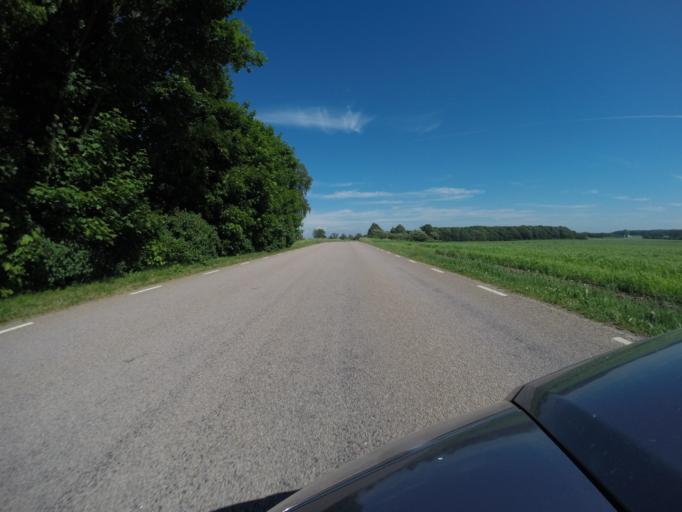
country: SE
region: Skane
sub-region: Helsingborg
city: Odakra
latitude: 56.1052
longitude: 12.7264
